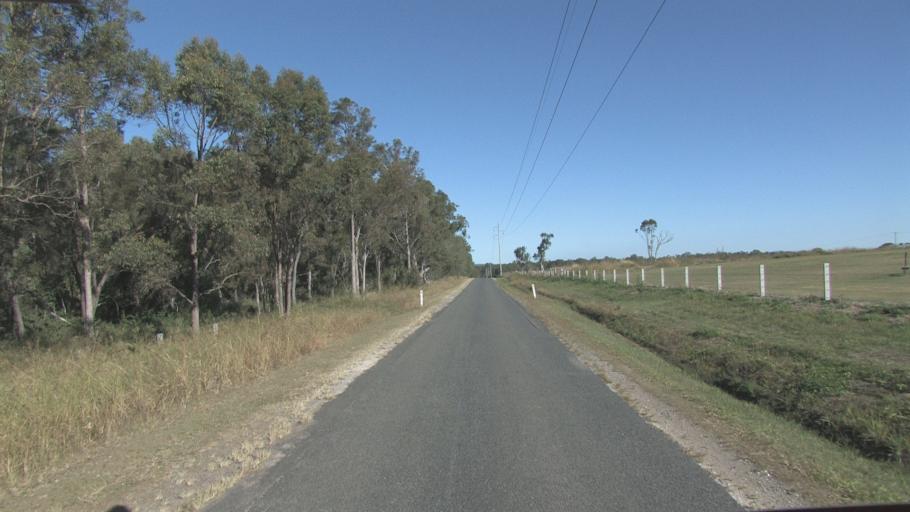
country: AU
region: Queensland
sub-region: Logan
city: Chambers Flat
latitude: -27.7723
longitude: 153.0595
